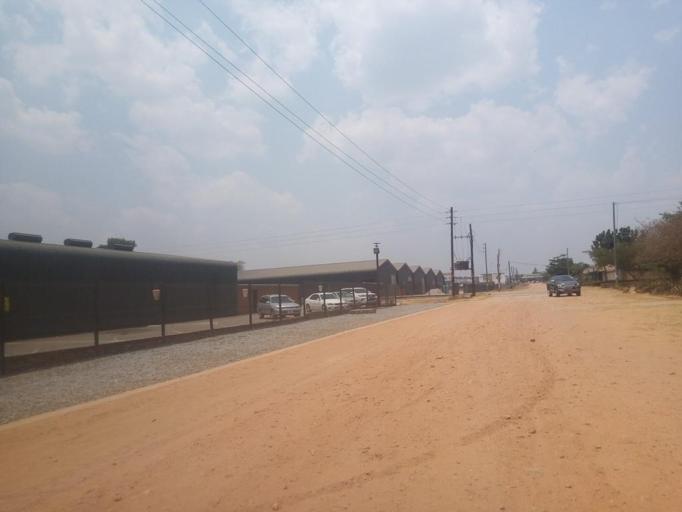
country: ZM
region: Lusaka
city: Lusaka
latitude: -15.3958
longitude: 28.3939
